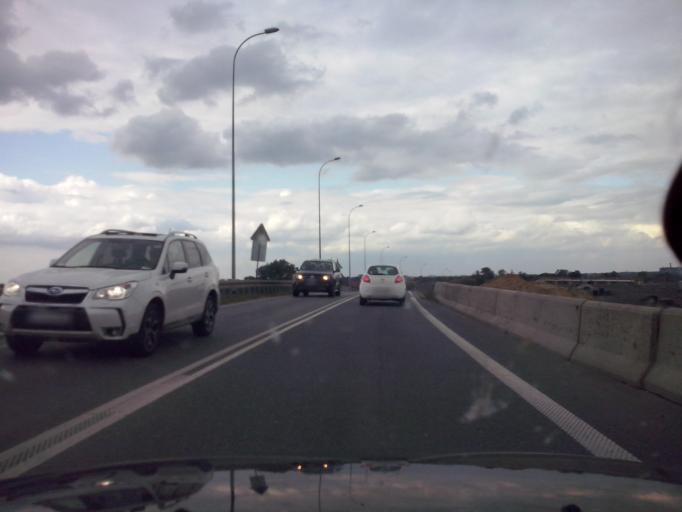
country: PL
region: Lesser Poland Voivodeship
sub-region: Powiat wielicki
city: Kokotow
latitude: 50.0346
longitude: 20.0631
